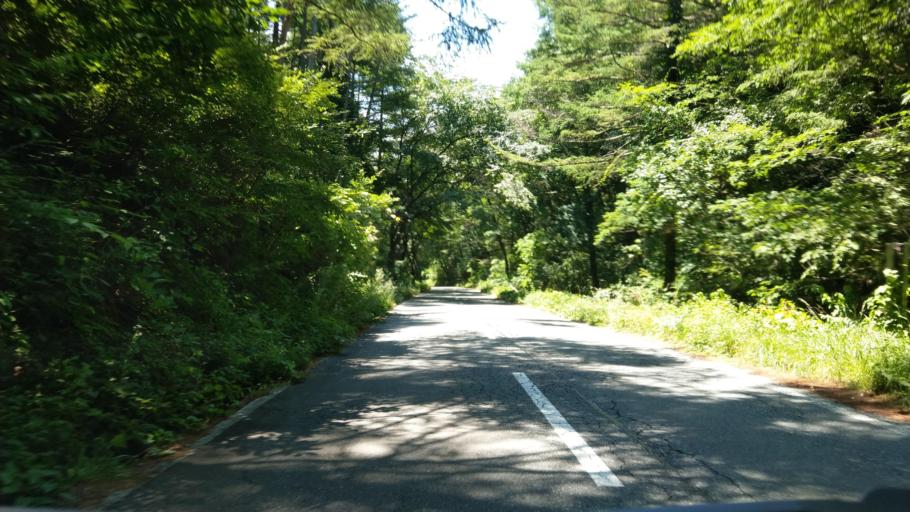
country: JP
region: Nagano
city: Komoro
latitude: 36.3784
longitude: 138.4643
